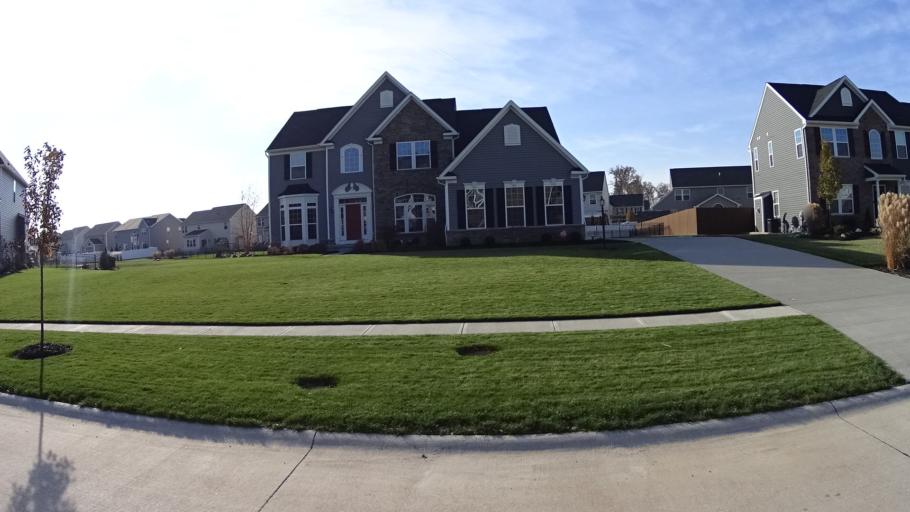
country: US
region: Ohio
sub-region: Lorain County
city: Avon
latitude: 41.4544
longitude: -82.0555
